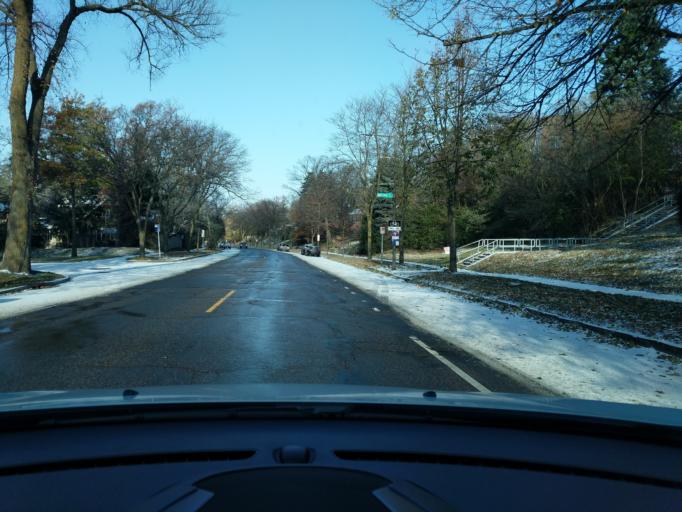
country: US
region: Minnesota
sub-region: Ramsey County
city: Lauderdale
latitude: 44.9843
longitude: -93.1975
